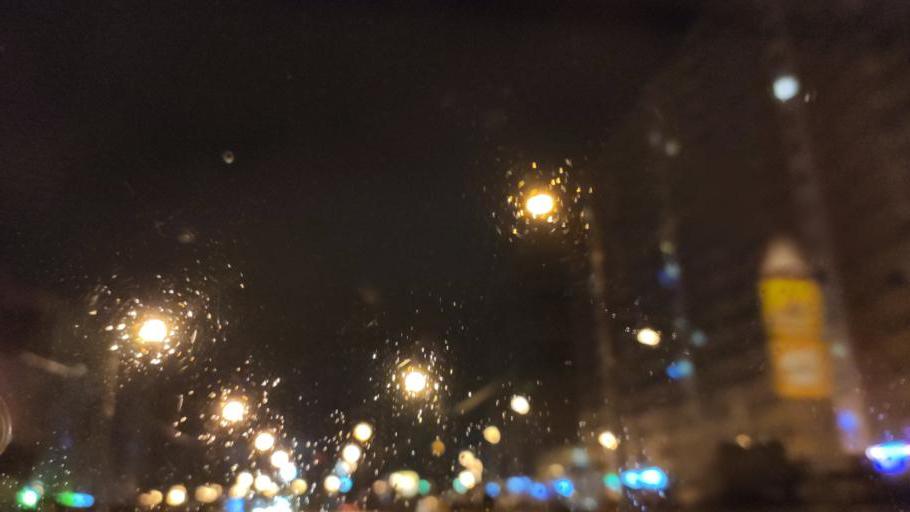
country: RU
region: Moskovskaya
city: Vatutinki
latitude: 55.5185
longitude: 37.3484
